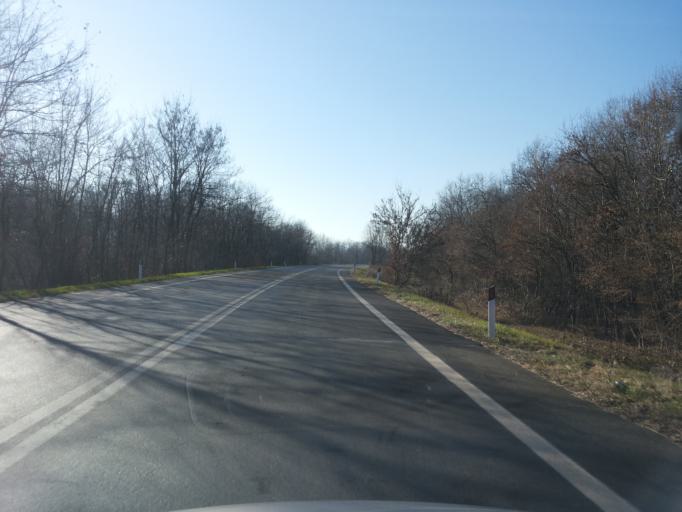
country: IT
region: Piedmont
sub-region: Provincia di Biella
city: Verrone
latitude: 45.4937
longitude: 8.1250
